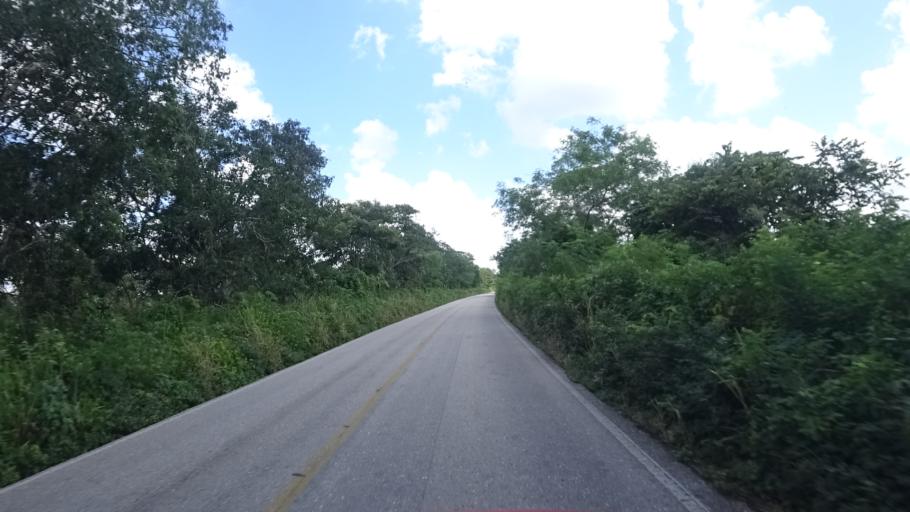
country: MX
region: Yucatan
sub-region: Panaba
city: Loche
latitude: 21.4074
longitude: -88.1430
